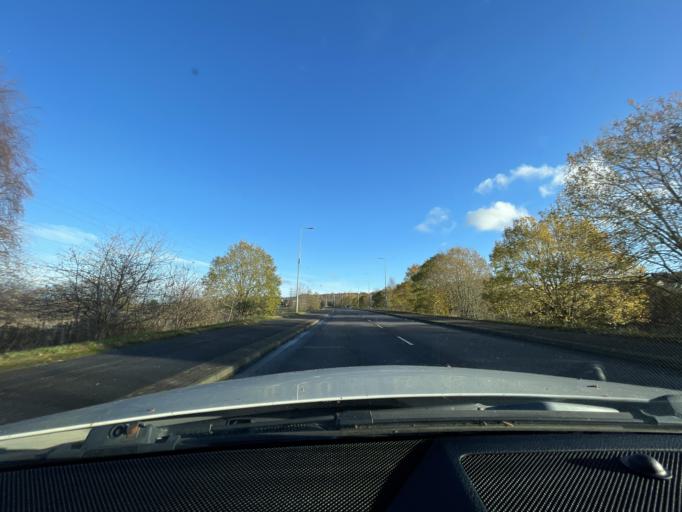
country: GB
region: Scotland
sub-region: Highland
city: Inverness
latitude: 57.4472
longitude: -4.2282
